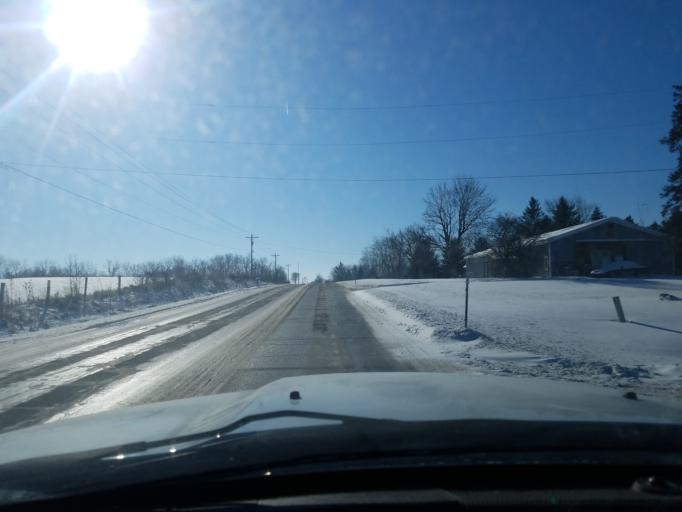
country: US
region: Indiana
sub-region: Noble County
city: Kendallville
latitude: 41.4272
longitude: -85.2326
